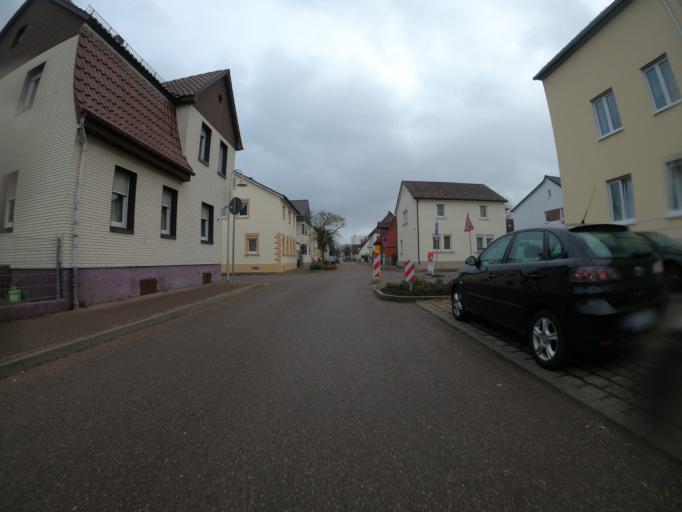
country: DE
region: Baden-Wuerttemberg
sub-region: Regierungsbezirk Stuttgart
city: Eislingen
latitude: 48.6935
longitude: 9.7123
